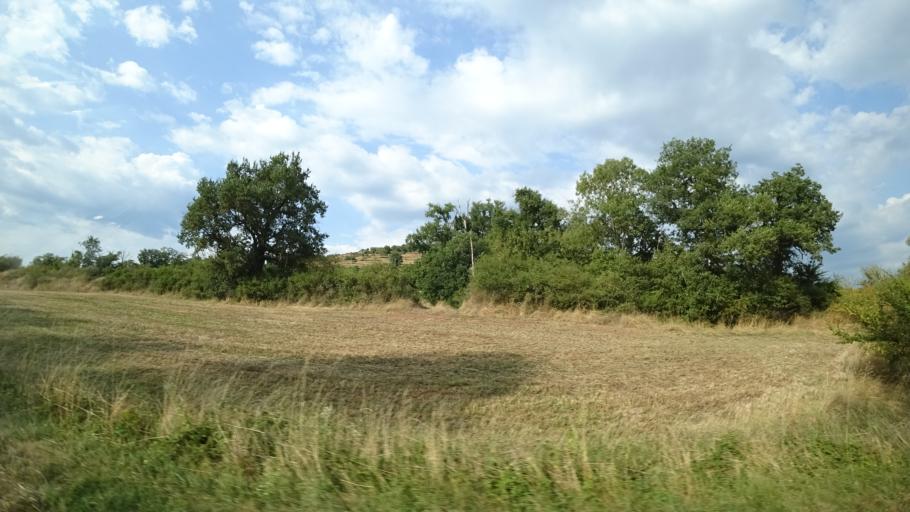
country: FR
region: Midi-Pyrenees
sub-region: Departement de l'Aveyron
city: Saint-Christophe-Vallon
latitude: 44.4868
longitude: 2.3953
